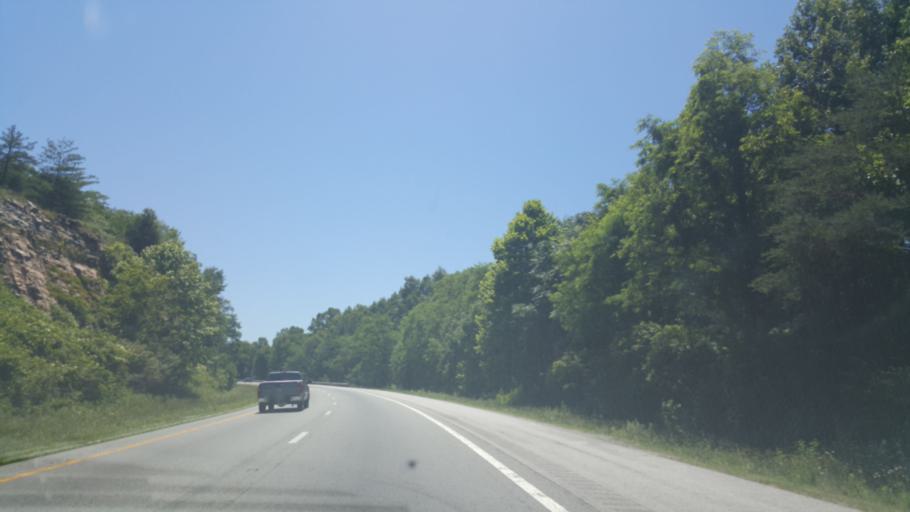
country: US
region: Tennessee
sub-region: Cumberland County
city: Fairfield Glade
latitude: 35.8901
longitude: -84.8404
